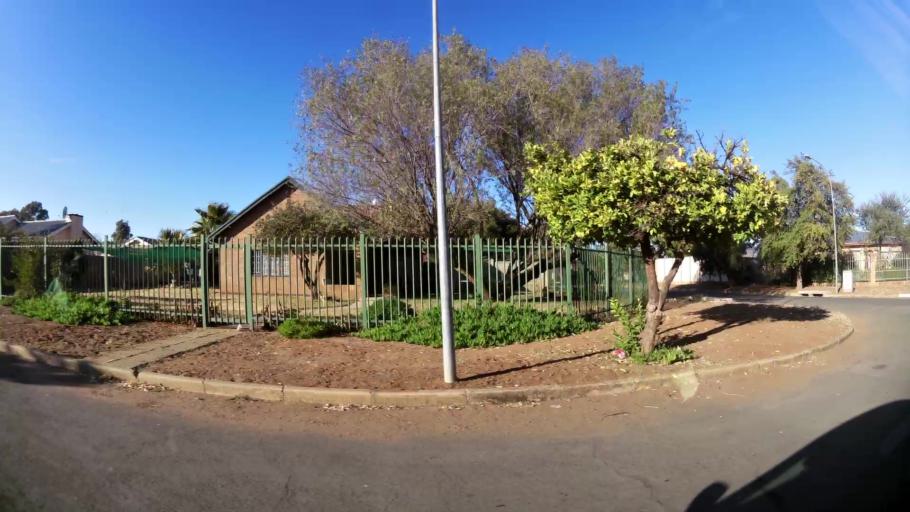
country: ZA
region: Northern Cape
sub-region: Frances Baard District Municipality
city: Kimberley
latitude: -28.7422
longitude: 24.7370
